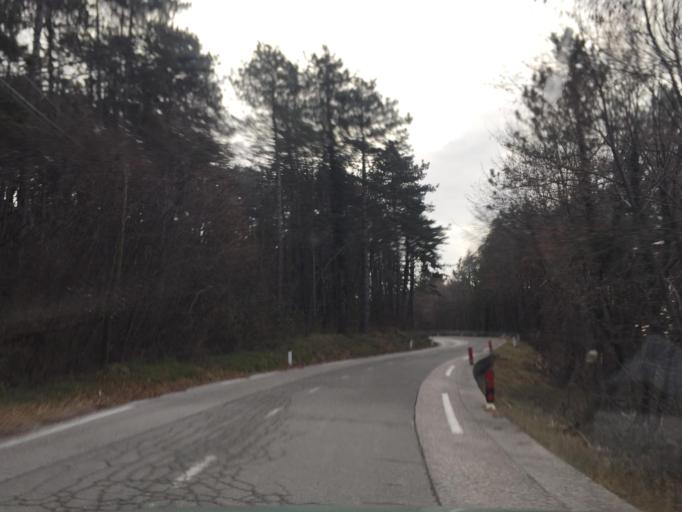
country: SI
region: Nova Gorica
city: Kromberk
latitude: 45.9784
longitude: 13.7160
